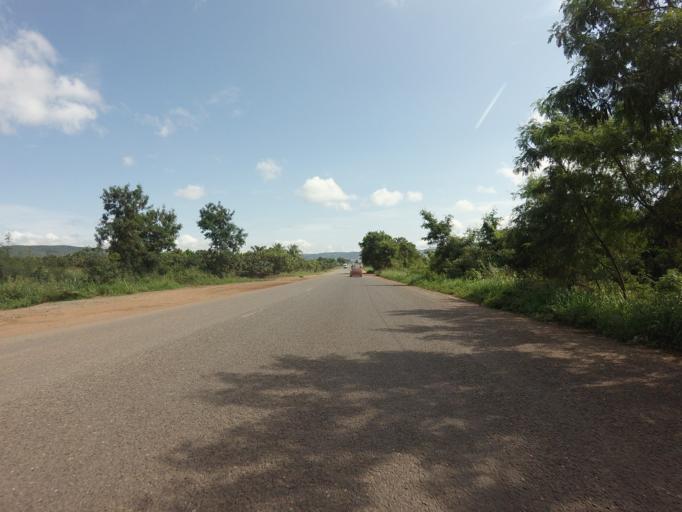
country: GH
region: Eastern
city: Aburi
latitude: 5.8289
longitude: -0.1185
